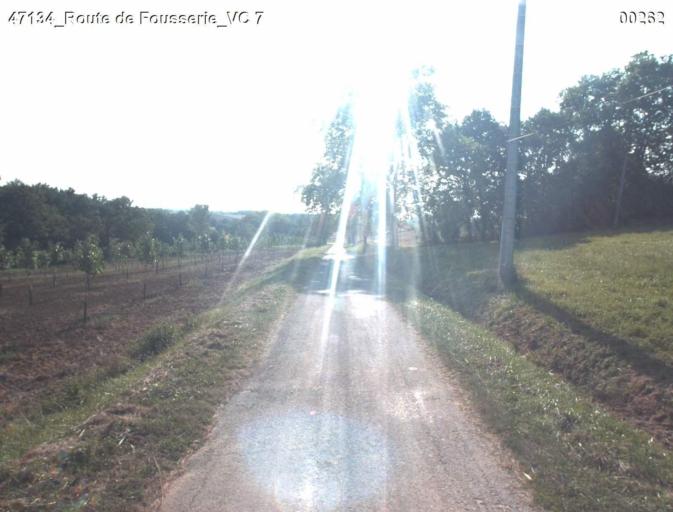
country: FR
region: Aquitaine
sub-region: Departement du Lot-et-Garonne
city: Mezin
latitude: 44.0150
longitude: 0.2682
